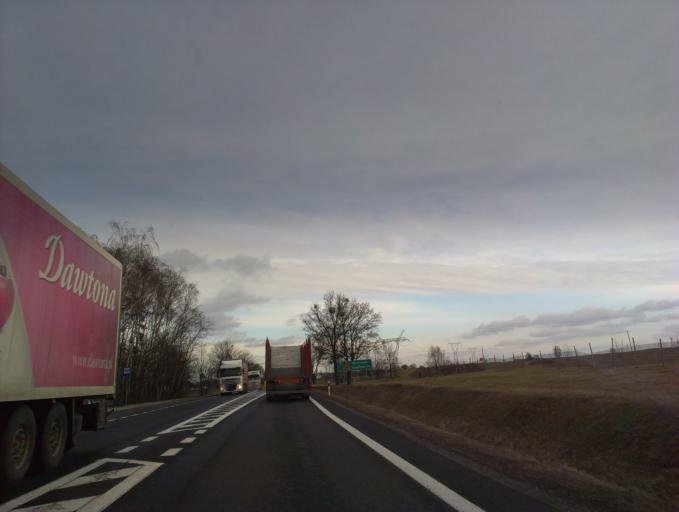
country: PL
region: Masovian Voivodeship
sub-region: Powiat sierpecki
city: Szczutowo
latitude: 52.9043
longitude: 19.4949
